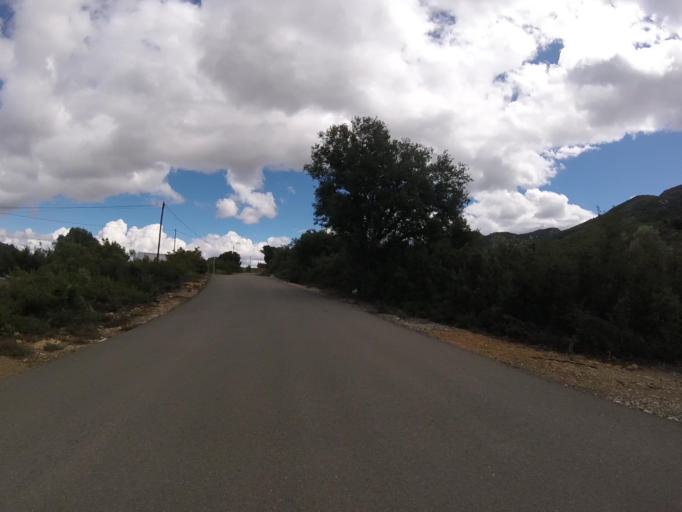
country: ES
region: Valencia
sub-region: Provincia de Castello
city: Sierra-Engarceran
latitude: 40.2949
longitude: -0.0450
